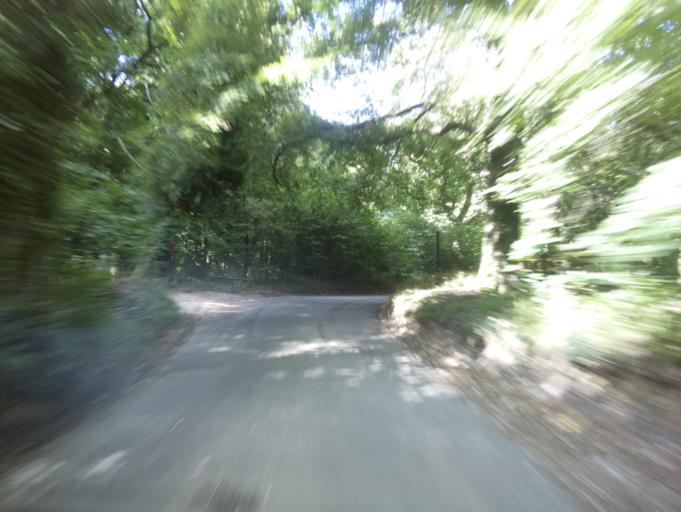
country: GB
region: England
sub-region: Hampshire
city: Chandlers Ford
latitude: 51.0639
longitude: -1.3803
